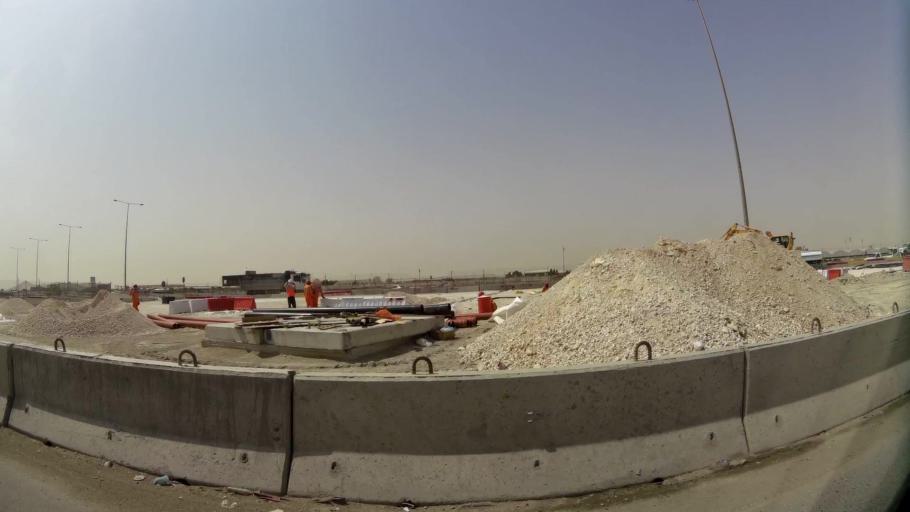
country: QA
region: Baladiyat ar Rayyan
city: Ar Rayyan
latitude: 25.2070
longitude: 51.4095
